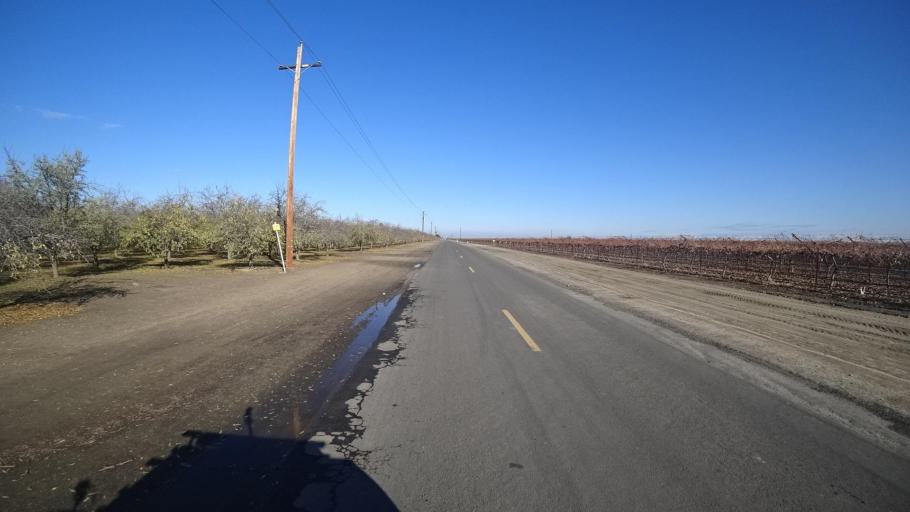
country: US
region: California
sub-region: Kern County
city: McFarland
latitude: 35.6934
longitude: -119.2764
